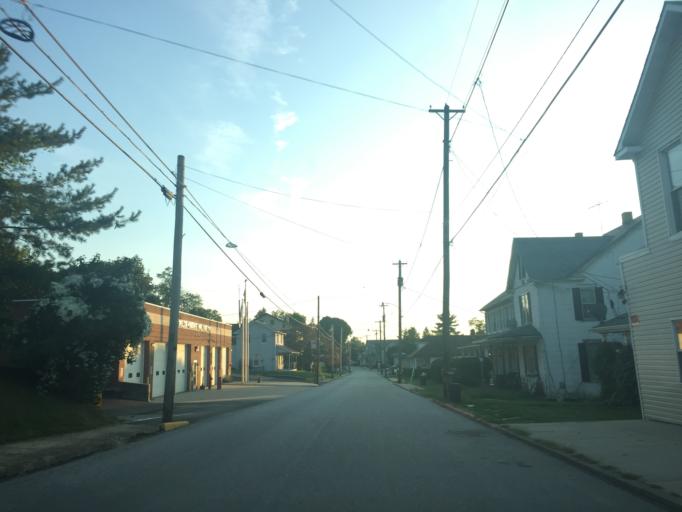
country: US
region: Pennsylvania
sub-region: York County
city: Susquehanna Trails
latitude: 39.7265
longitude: -76.3282
